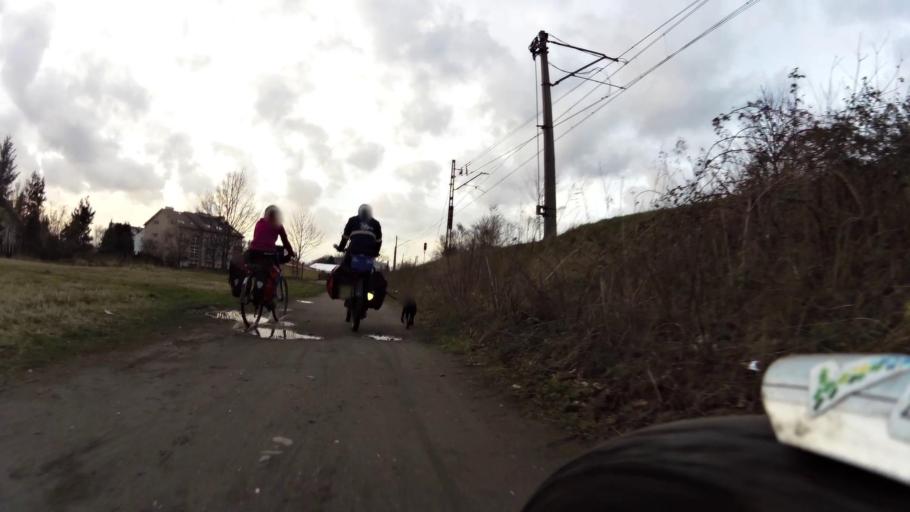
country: PL
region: West Pomeranian Voivodeship
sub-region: Powiat kamienski
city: Kamien Pomorski
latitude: 53.9612
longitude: 14.7714
